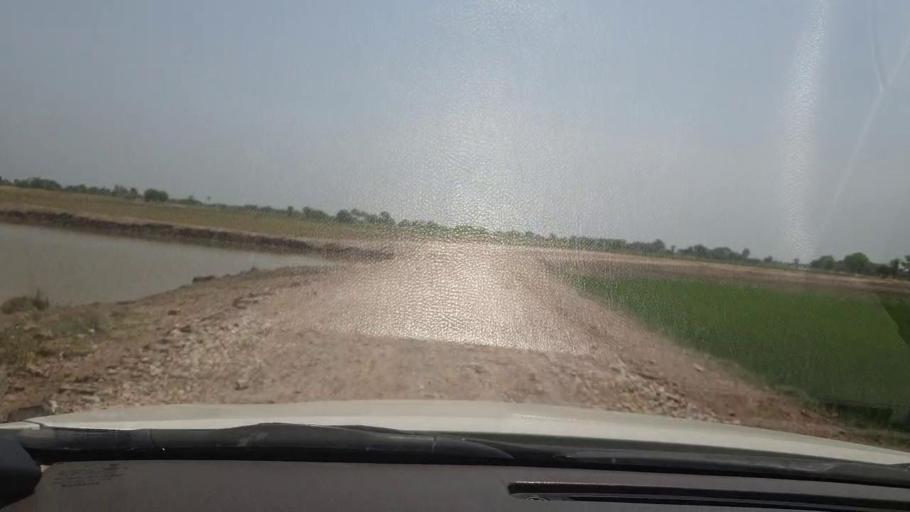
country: PK
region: Sindh
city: Garhi Yasin
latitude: 27.9168
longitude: 68.5558
